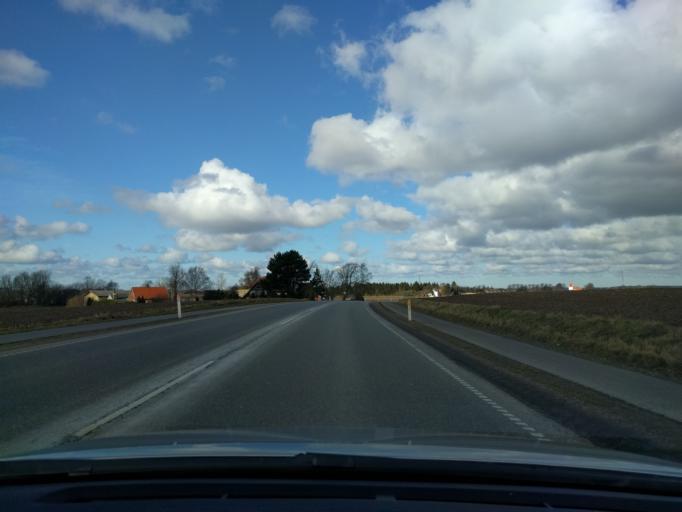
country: DK
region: Zealand
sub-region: Guldborgsund Kommune
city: Norre Alslev
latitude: 54.8370
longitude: 11.8604
